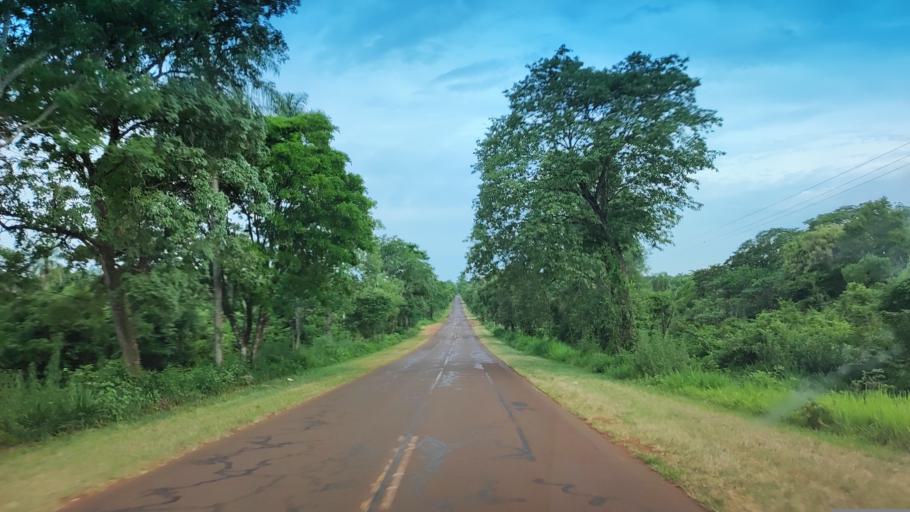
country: AR
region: Misiones
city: Gobernador Roca
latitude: -27.1382
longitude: -55.5011
